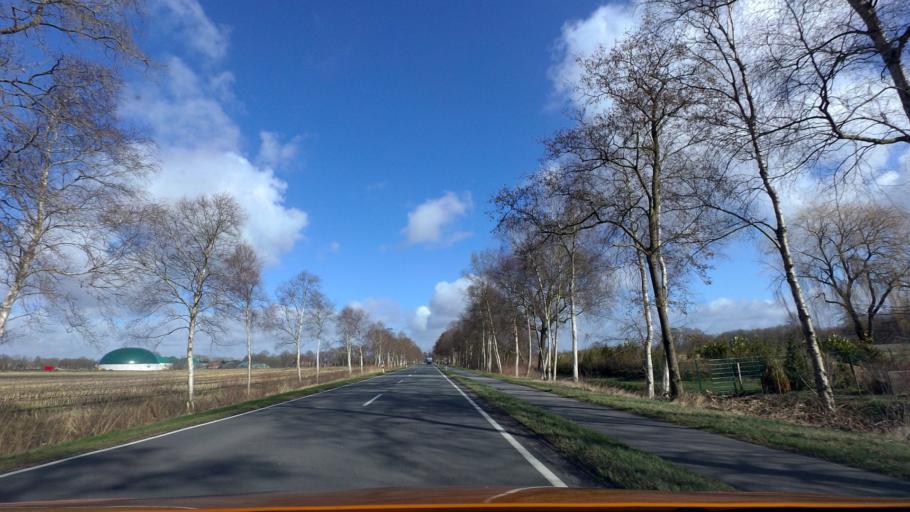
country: DE
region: Lower Saxony
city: Edewecht
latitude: 53.0950
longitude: 7.9464
